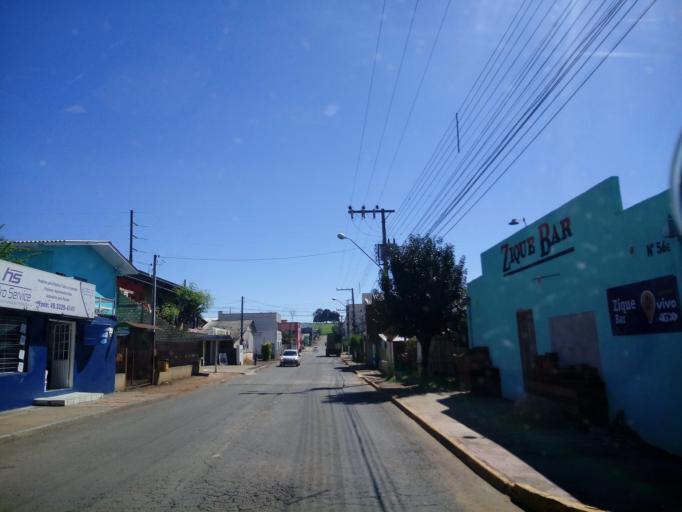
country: BR
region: Santa Catarina
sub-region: Chapeco
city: Chapeco
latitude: -27.0912
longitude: -52.6740
